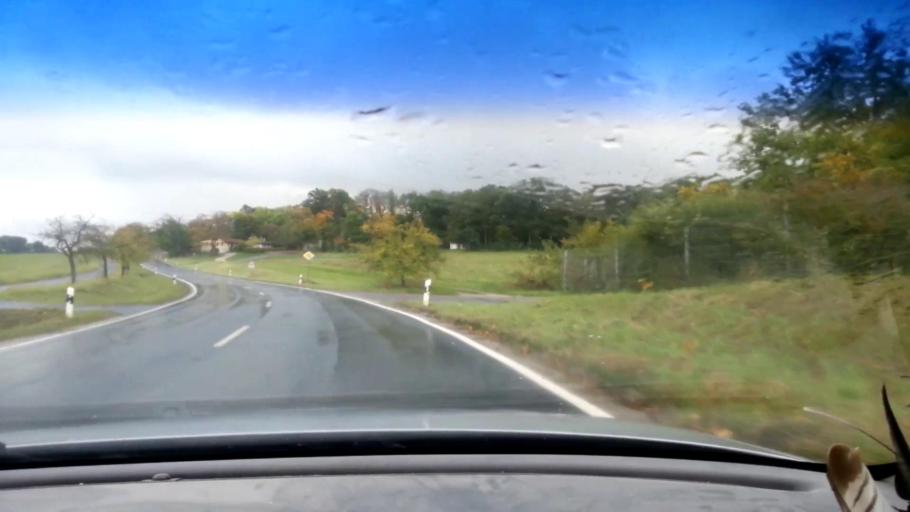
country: DE
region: Bavaria
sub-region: Upper Franconia
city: Burgebrach
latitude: 49.8431
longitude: 10.7316
